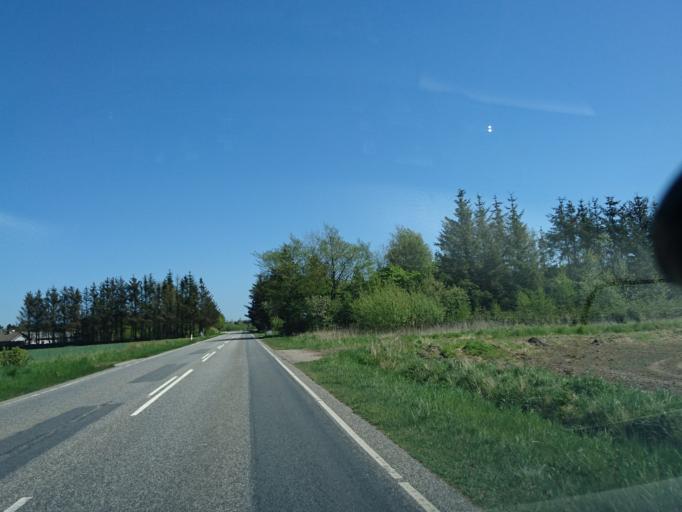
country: DK
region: North Denmark
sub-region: Hjorring Kommune
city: Sindal
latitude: 57.5766
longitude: 10.1615
